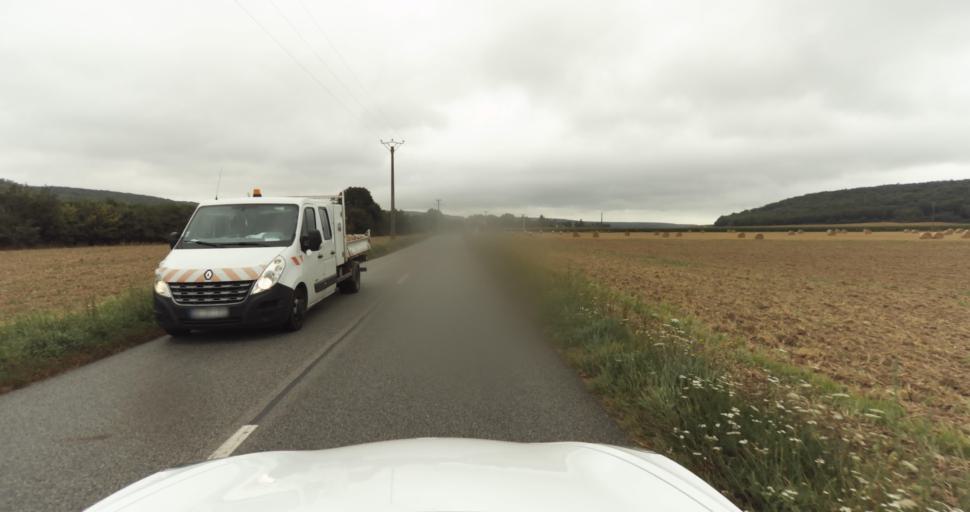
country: FR
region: Haute-Normandie
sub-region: Departement de l'Eure
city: Normanville
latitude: 49.0791
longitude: 1.1448
